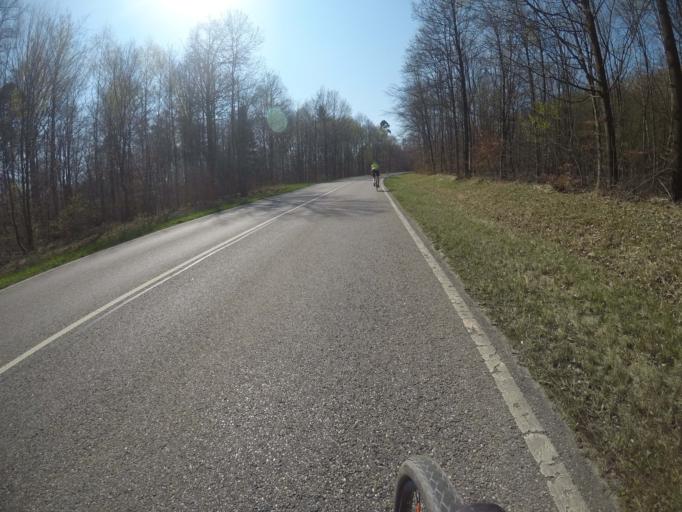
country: DE
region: Baden-Wuerttemberg
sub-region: Regierungsbezirk Stuttgart
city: Leonberg
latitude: 48.7552
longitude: 9.0383
